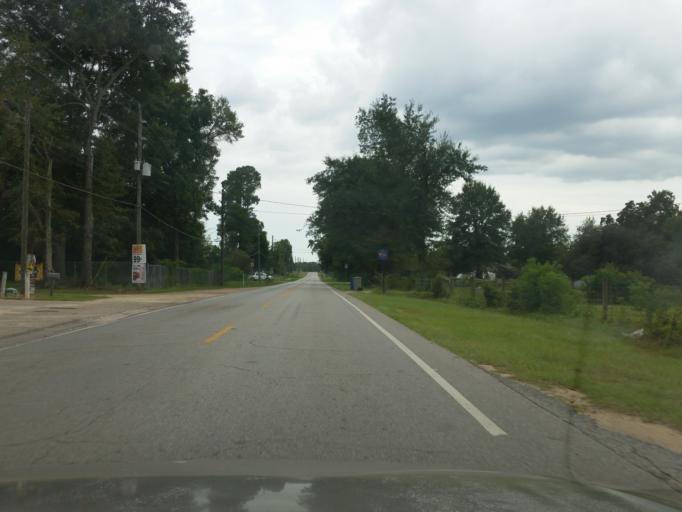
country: US
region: Florida
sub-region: Escambia County
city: Molino
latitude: 30.7176
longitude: -87.3387
